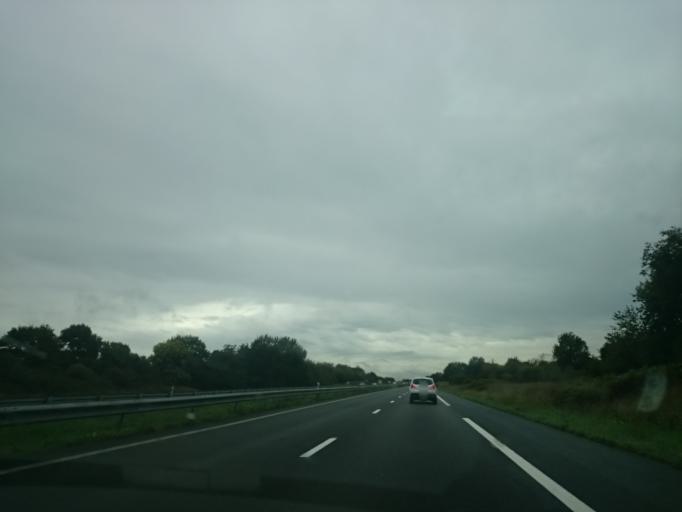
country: FR
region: Pays de la Loire
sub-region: Departement de la Loire-Atlantique
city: Le Temple-de-Bretagne
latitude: 47.3194
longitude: -1.7742
